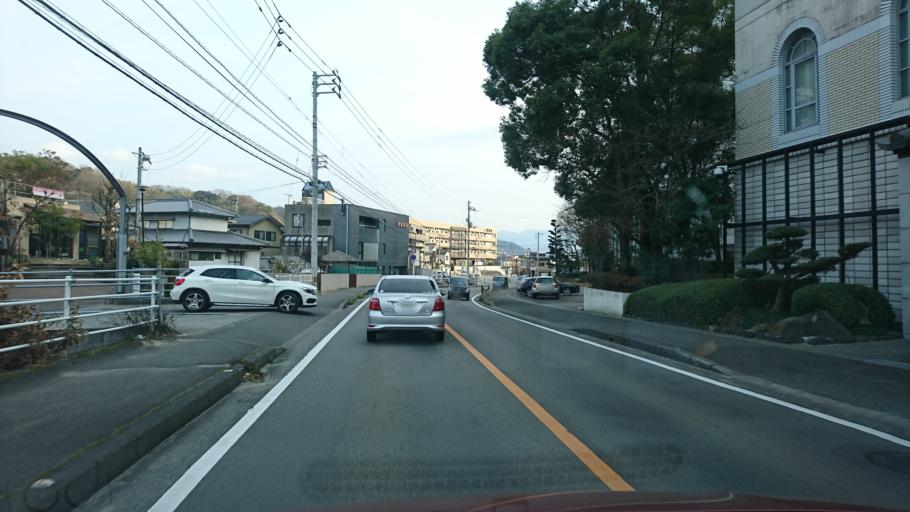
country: JP
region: Ehime
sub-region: Shikoku-chuo Shi
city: Matsuyama
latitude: 33.8622
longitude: 132.7749
